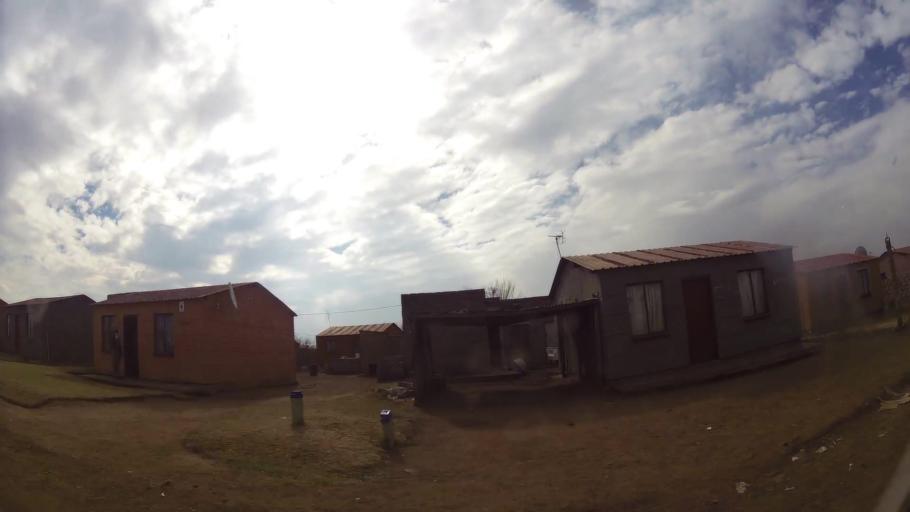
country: ZA
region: Gauteng
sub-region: Ekurhuleni Metropolitan Municipality
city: Germiston
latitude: -26.4117
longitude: 28.1637
